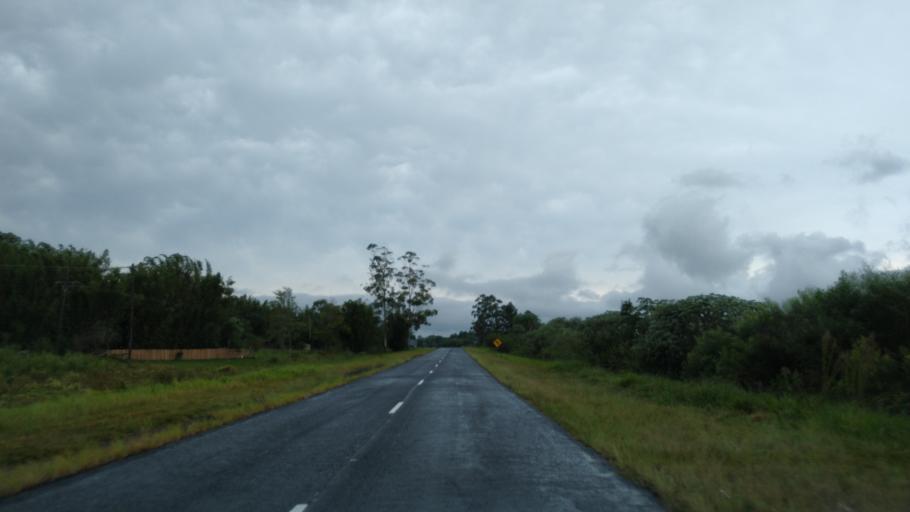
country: AR
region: Corrientes
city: Loreto
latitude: -27.7779
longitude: -57.2763
